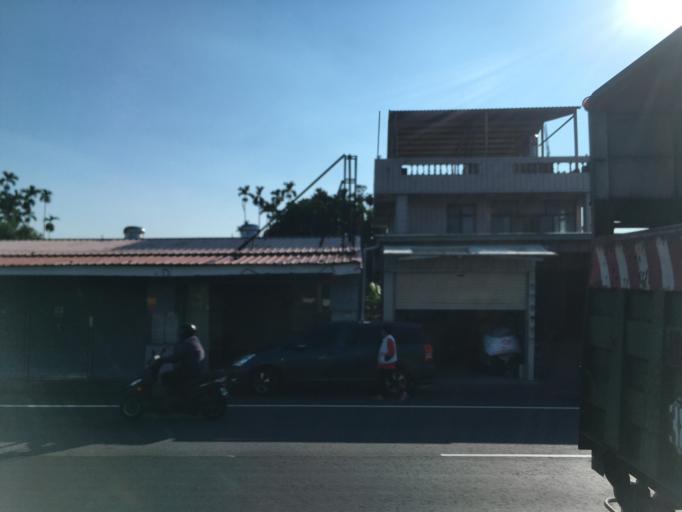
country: TW
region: Taiwan
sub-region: Chiayi
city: Jiayi Shi
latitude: 23.4432
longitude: 120.5115
